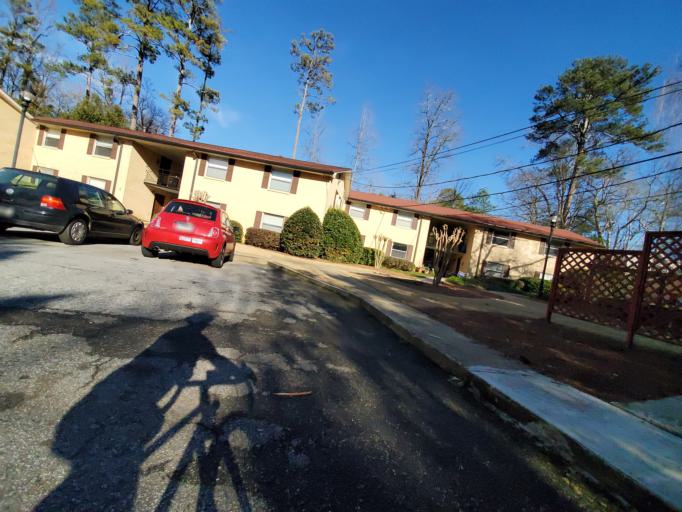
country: US
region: Georgia
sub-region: DeKalb County
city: North Decatur
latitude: 33.7859
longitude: -84.3001
